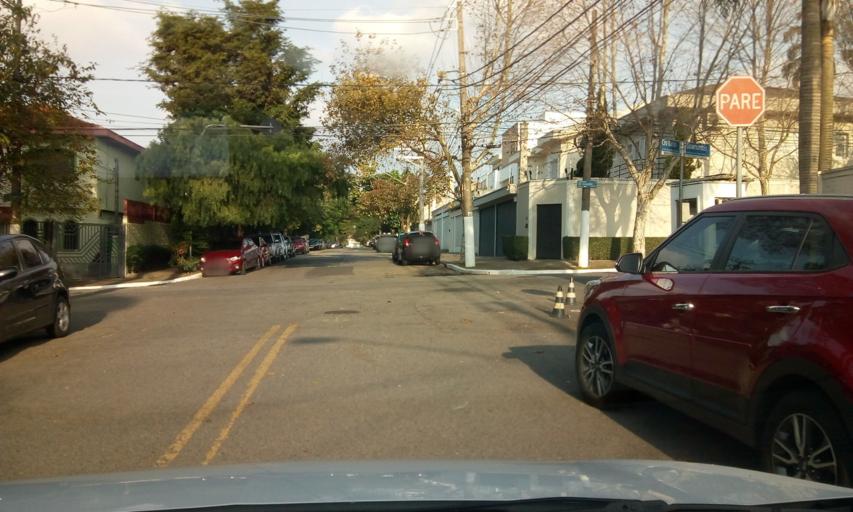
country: BR
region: Sao Paulo
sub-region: Sao Paulo
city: Sao Paulo
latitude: -23.6146
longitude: -46.6548
